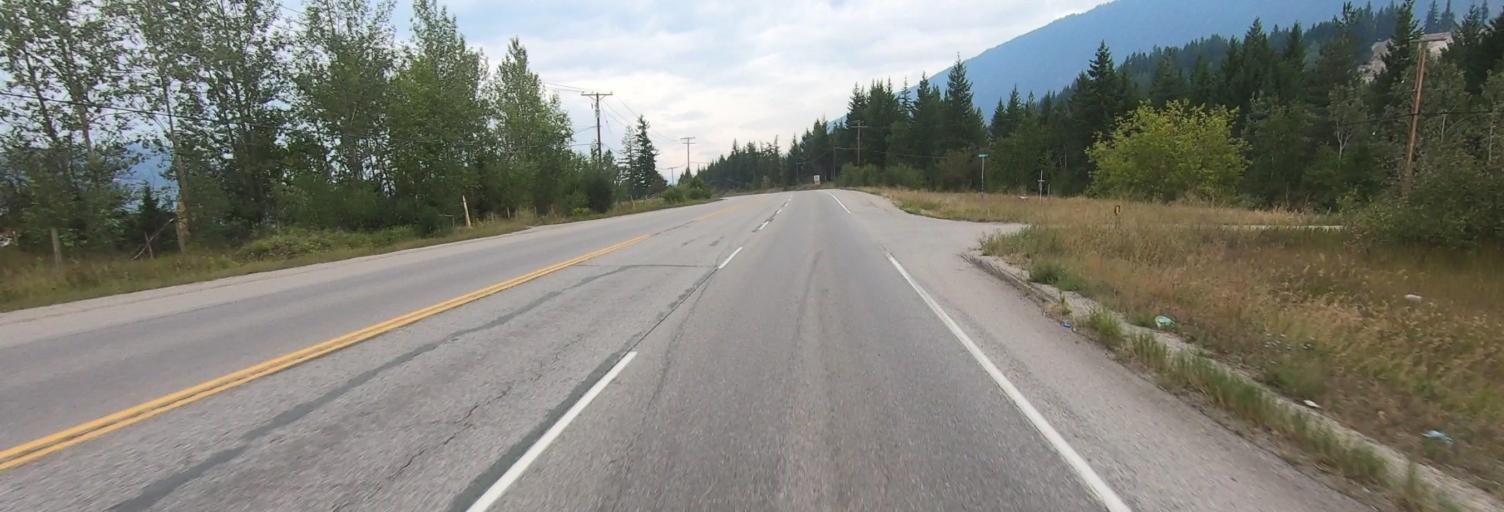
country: CA
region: British Columbia
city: Salmon Arm
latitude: 50.7971
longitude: -119.3263
